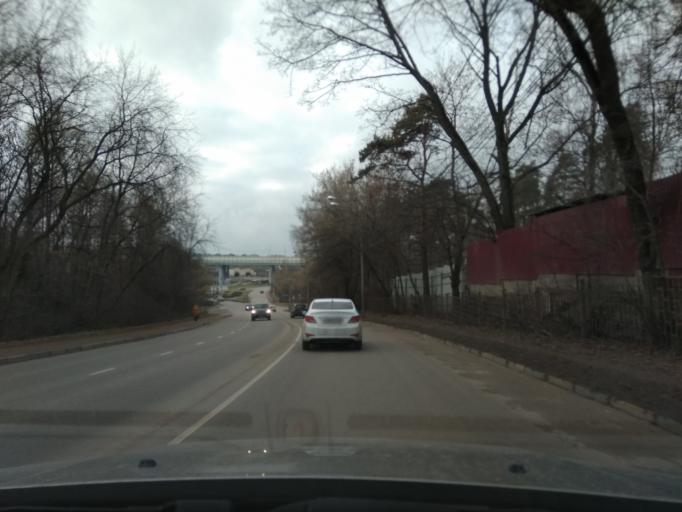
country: RU
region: Moskovskaya
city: Vidnoye
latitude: 55.5535
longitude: 37.6886
